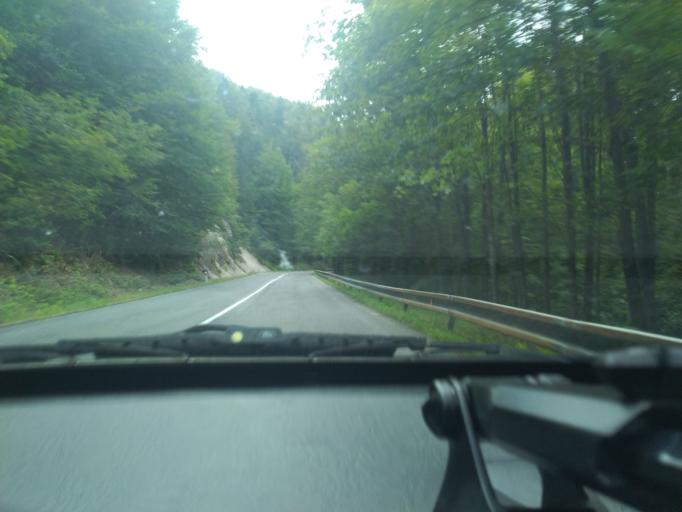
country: SK
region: Banskobystricky
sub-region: Okres Banska Bystrica
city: Banska Bystrica
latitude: 48.8222
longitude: 19.0218
